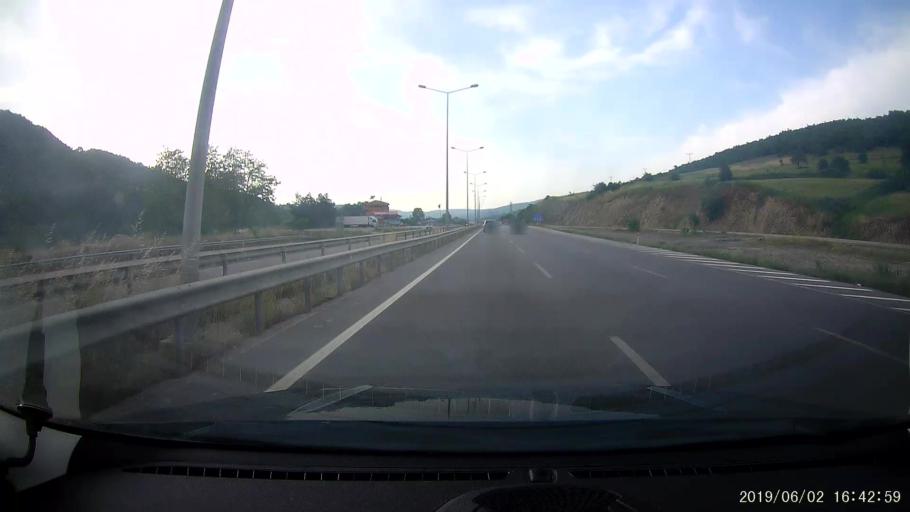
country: TR
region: Samsun
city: Kavak
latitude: 41.1276
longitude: 36.1367
